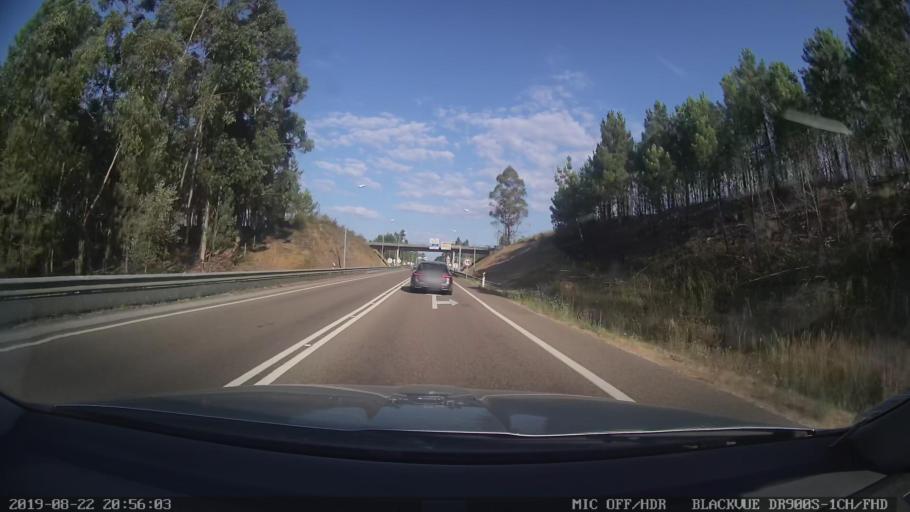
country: PT
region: Castelo Branco
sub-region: Serta
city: Serta
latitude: 39.7862
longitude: -8.0436
